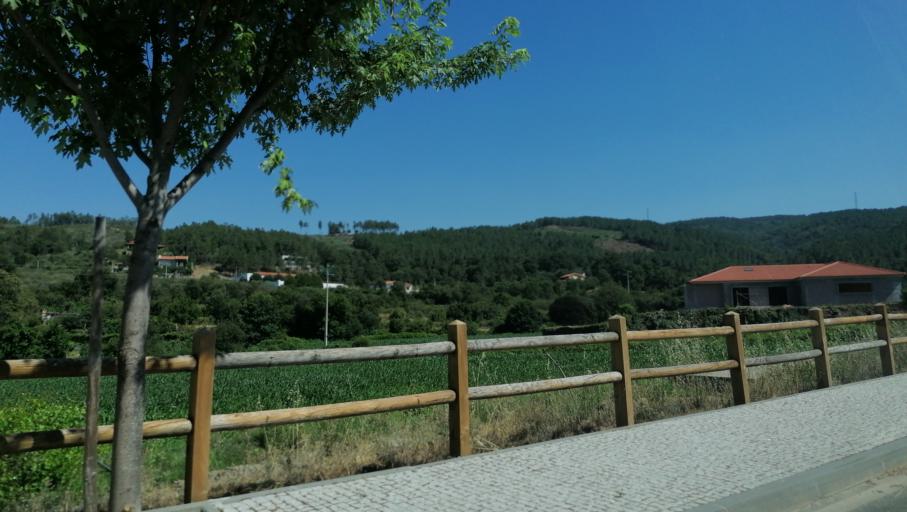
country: PT
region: Viseu
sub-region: Tarouca
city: Tarouca
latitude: 41.0206
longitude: -7.7714
